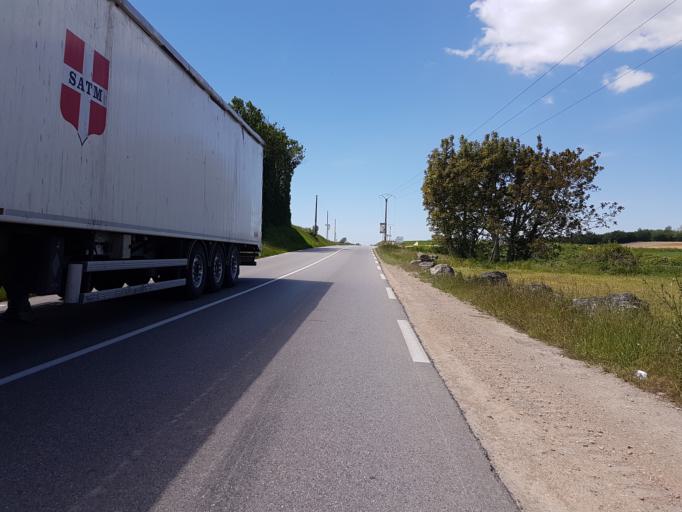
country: FR
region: Rhone-Alpes
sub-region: Departement de l'Isere
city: Chavanoz
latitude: 45.7801
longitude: 5.1702
